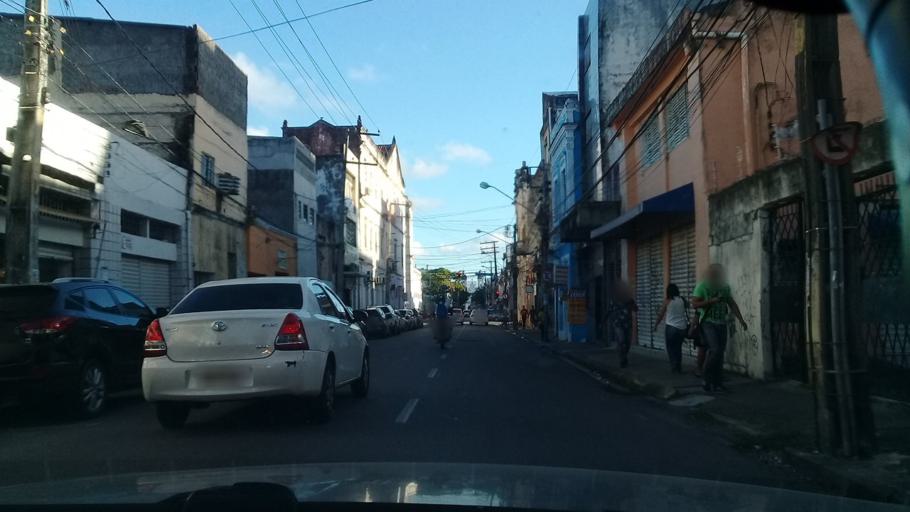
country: BR
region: Pernambuco
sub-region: Recife
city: Recife
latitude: -8.0612
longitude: -34.8875
